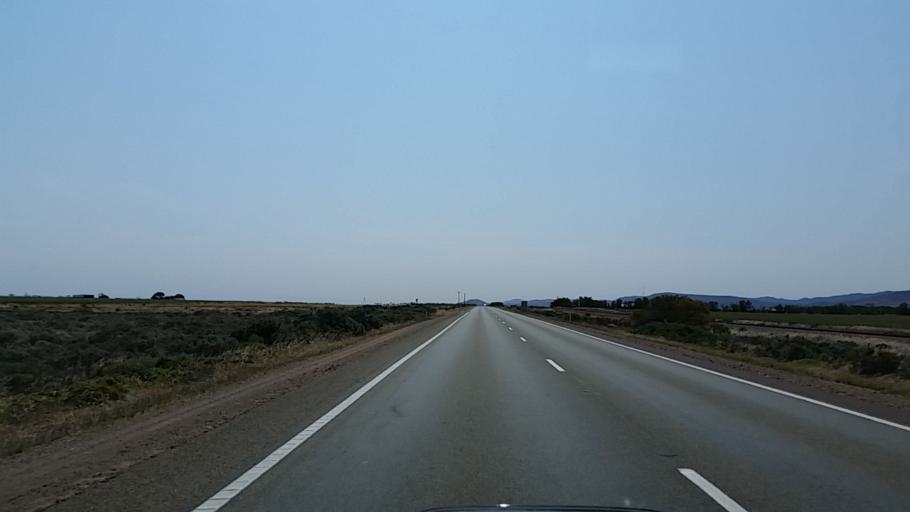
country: AU
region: South Australia
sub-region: Port Pirie City and Dists
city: Port Pirie
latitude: -32.9618
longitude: 137.9825
